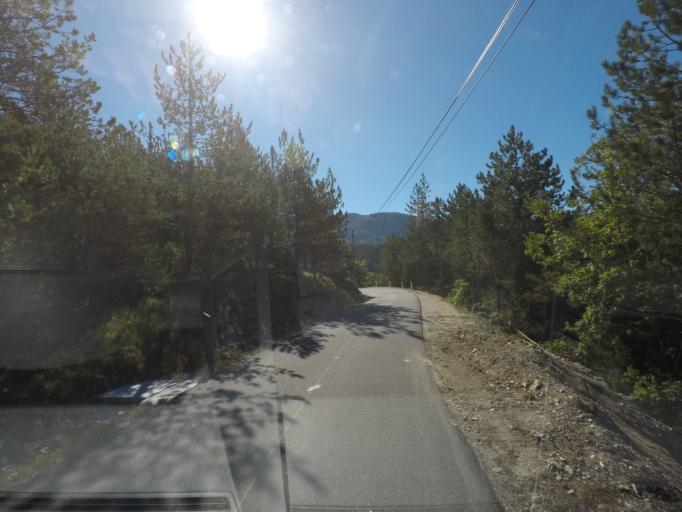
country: FR
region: Rhone-Alpes
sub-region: Departement de la Drome
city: Die
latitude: 44.6210
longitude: 5.2986
